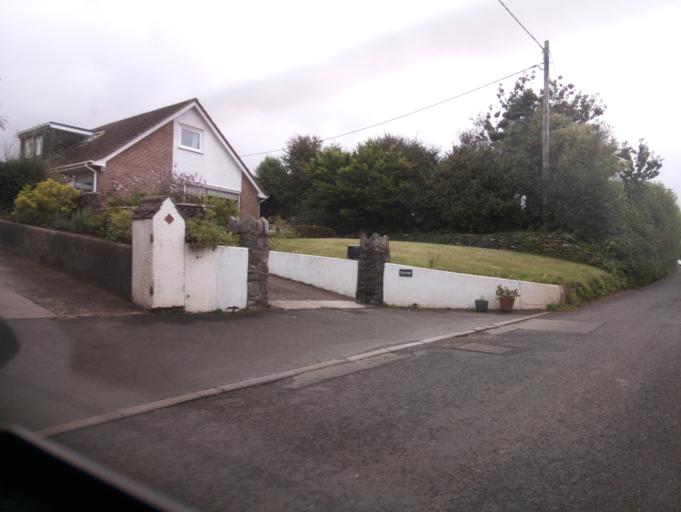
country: GB
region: England
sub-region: Devon
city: Salcombe
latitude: 50.2731
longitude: -3.6809
